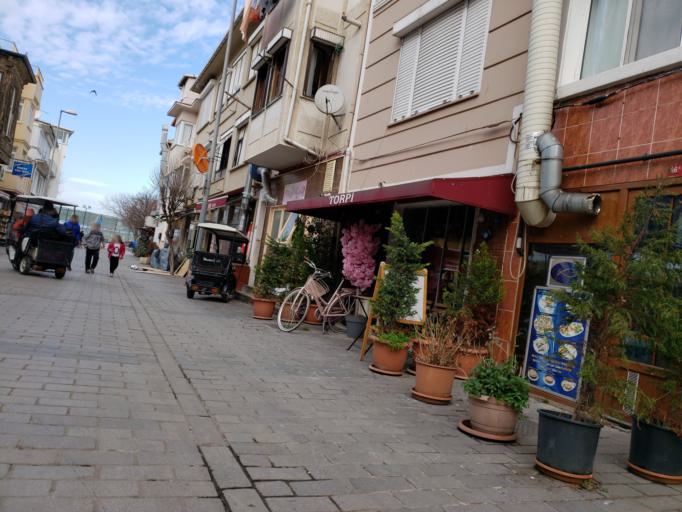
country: TR
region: Istanbul
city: Adalan
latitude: 40.8780
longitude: 29.0998
